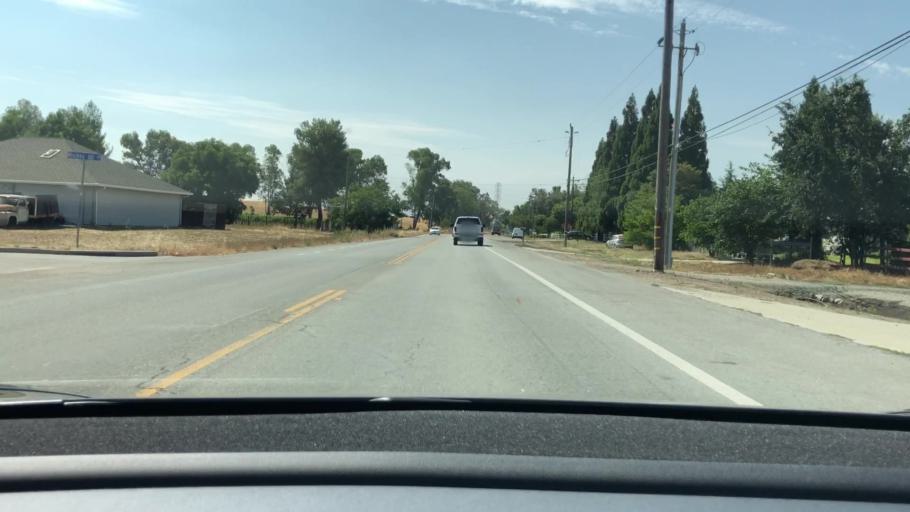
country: US
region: California
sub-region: Santa Clara County
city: San Martin
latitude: 37.0417
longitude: -121.5992
